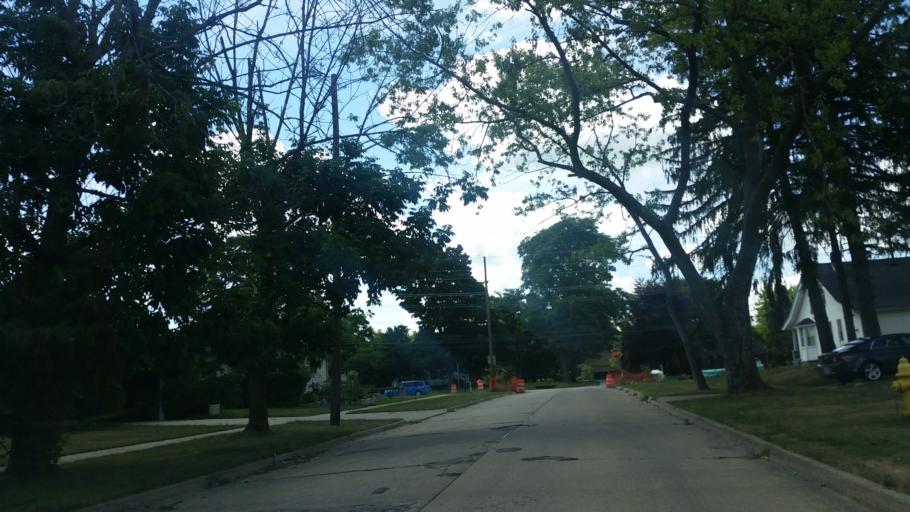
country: US
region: Ohio
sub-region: Cuyahoga County
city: Parma Heights
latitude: 41.3647
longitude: -81.7781
